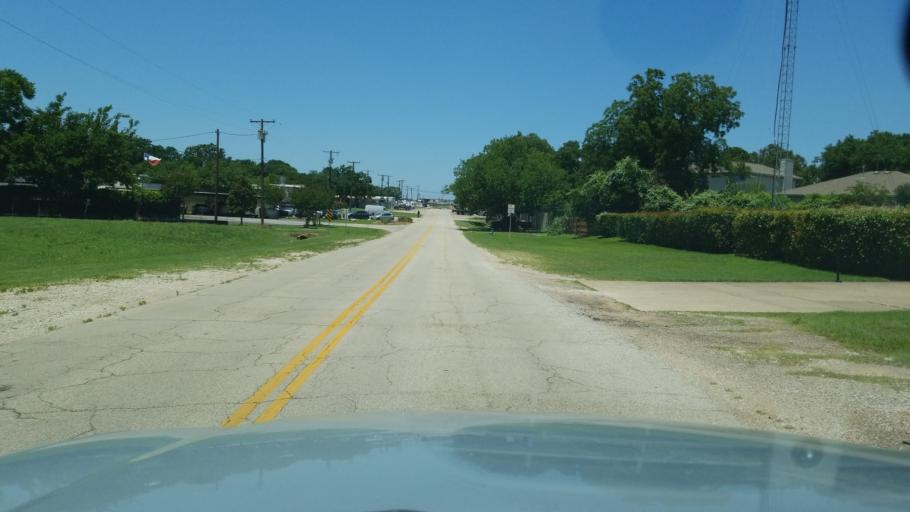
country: US
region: Texas
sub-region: Dallas County
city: Irving
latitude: 32.8039
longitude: -96.9174
